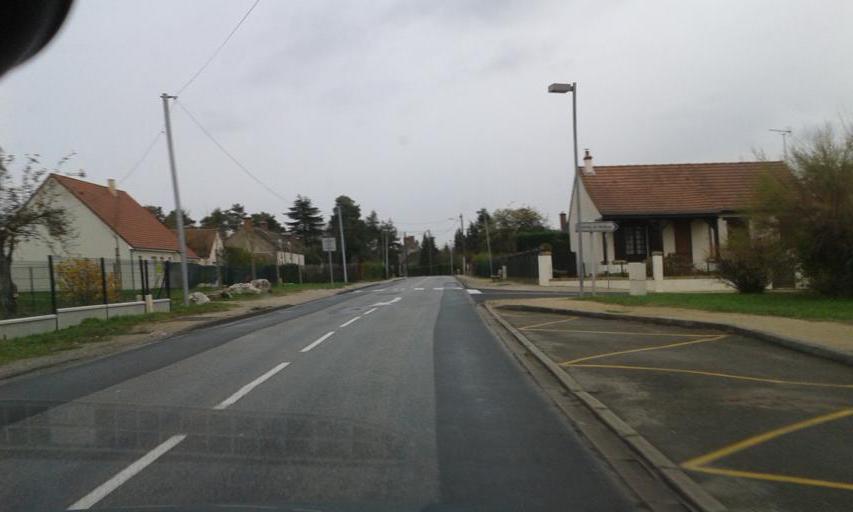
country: FR
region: Centre
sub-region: Departement du Loiret
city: Vitry-aux-Loges
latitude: 47.9316
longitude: 2.2616
